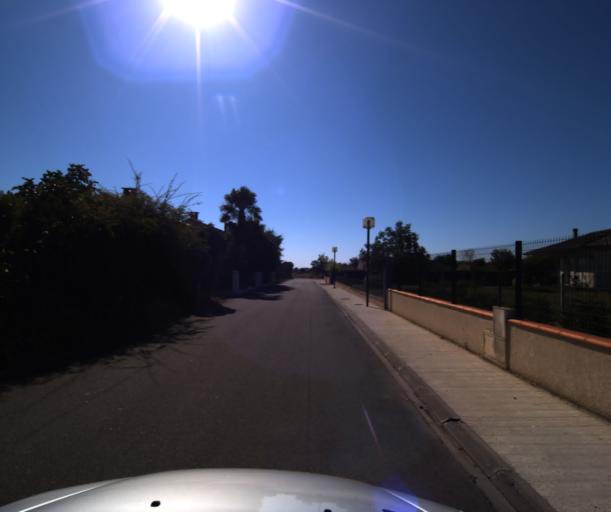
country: FR
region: Midi-Pyrenees
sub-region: Departement de la Haute-Garonne
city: Eaunes
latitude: 43.4214
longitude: 1.3549
